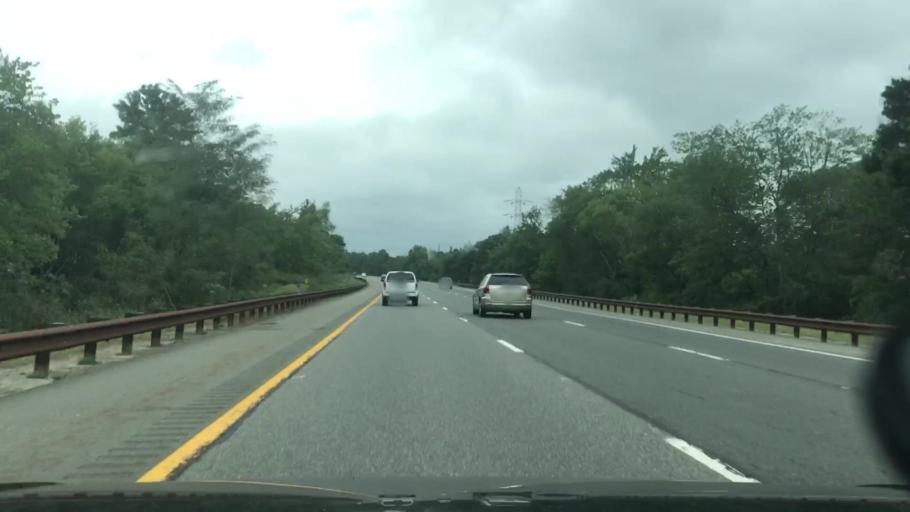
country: US
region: New Jersey
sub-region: Ocean County
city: Waretown
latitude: 39.8145
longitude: -74.2291
